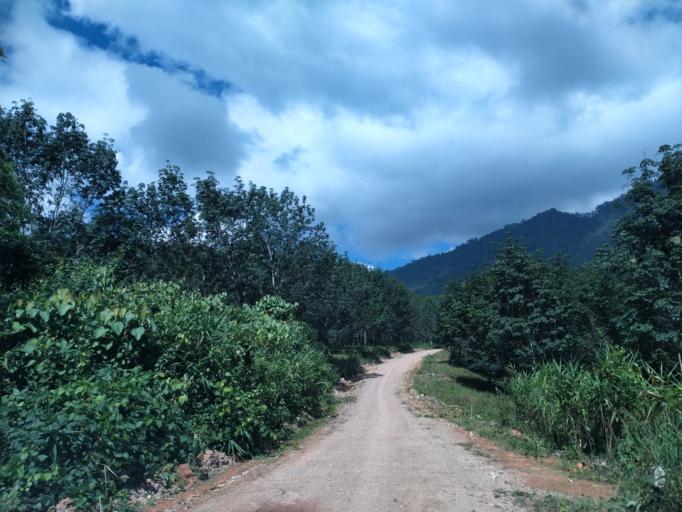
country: TH
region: Nong Khai
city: Rattanawapi
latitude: 18.6385
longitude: 102.9322
